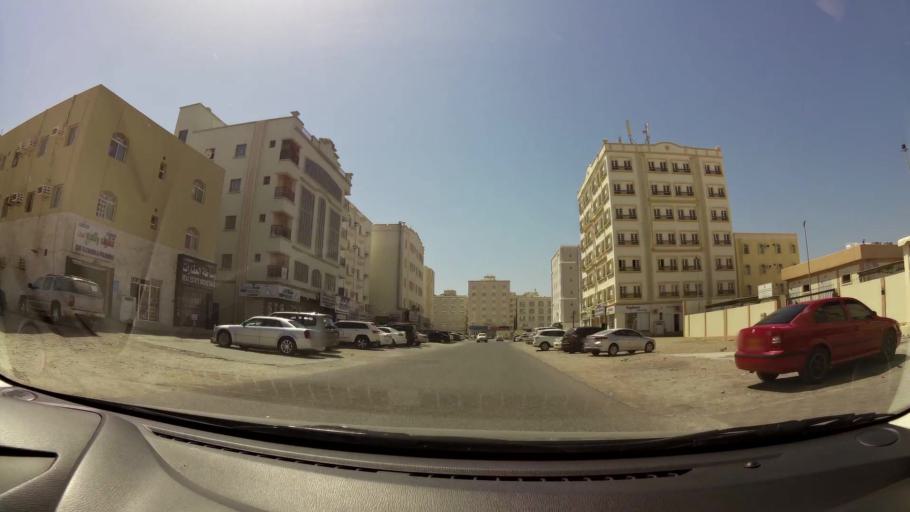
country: OM
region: Muhafazat Masqat
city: As Sib al Jadidah
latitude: 23.6250
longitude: 58.2195
